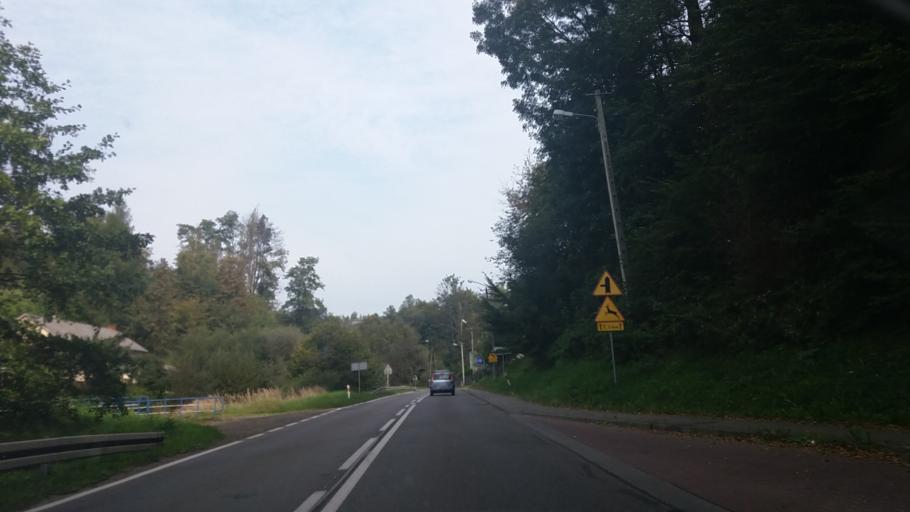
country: PL
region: Lesser Poland Voivodeship
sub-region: Powiat chrzanowski
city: Plaza
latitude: 50.0855
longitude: 19.4549
